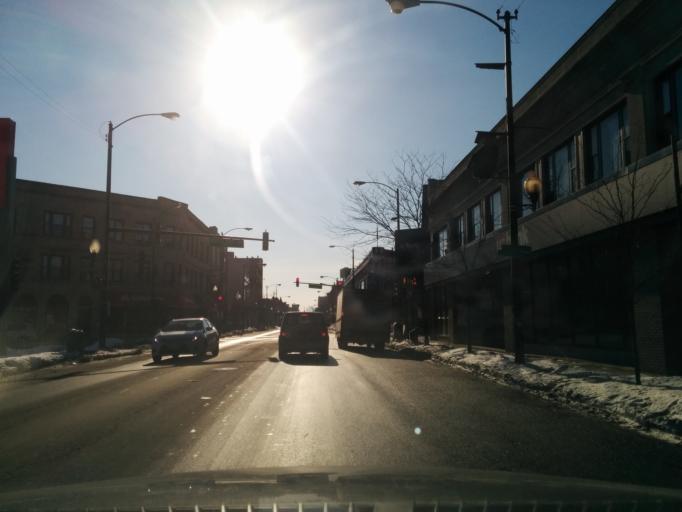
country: US
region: Illinois
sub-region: Cook County
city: Lincolnwood
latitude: 41.9360
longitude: -87.7189
